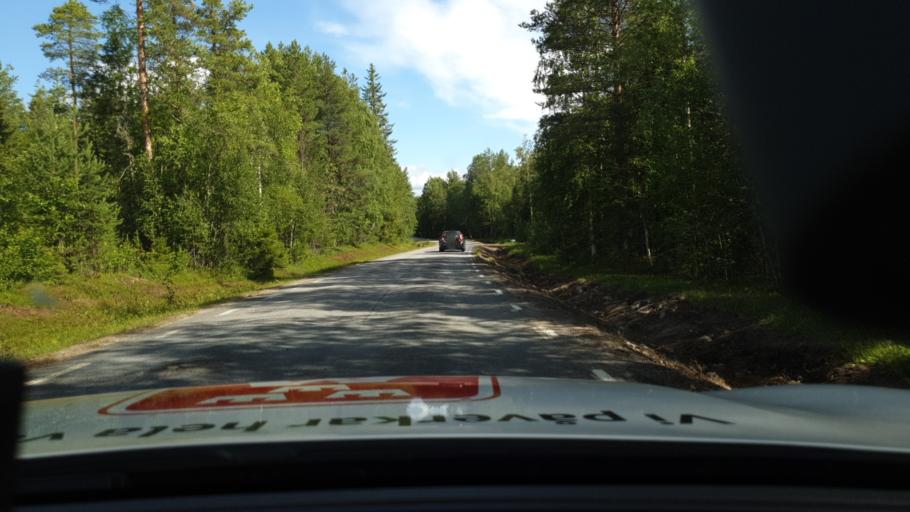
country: SE
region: Norrbotten
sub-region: Lulea Kommun
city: Ranea
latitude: 65.7855
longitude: 22.2970
